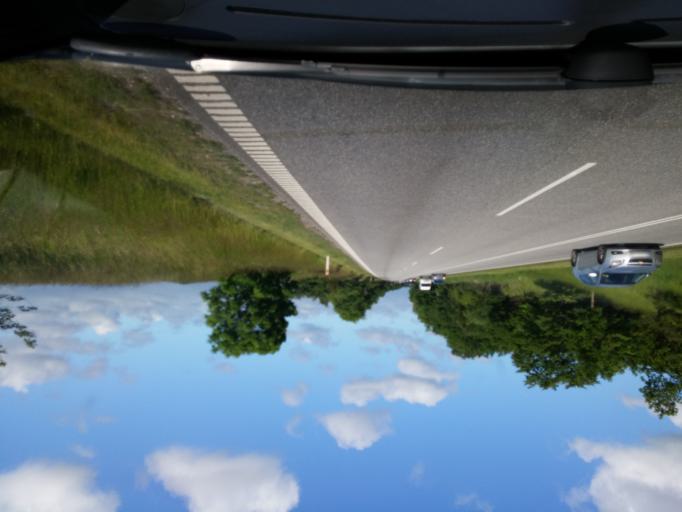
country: DK
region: Capital Region
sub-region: Hillerod Kommune
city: Hillerod
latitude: 55.8908
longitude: 12.2911
